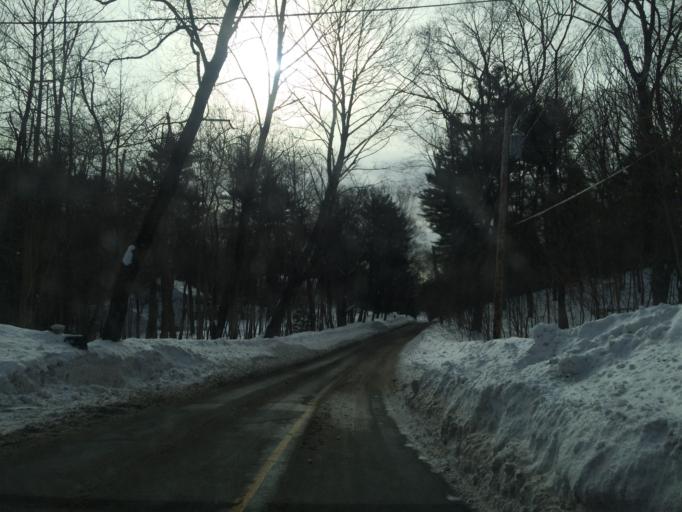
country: US
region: Massachusetts
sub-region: Middlesex County
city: Weston
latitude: 42.3593
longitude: -71.2734
